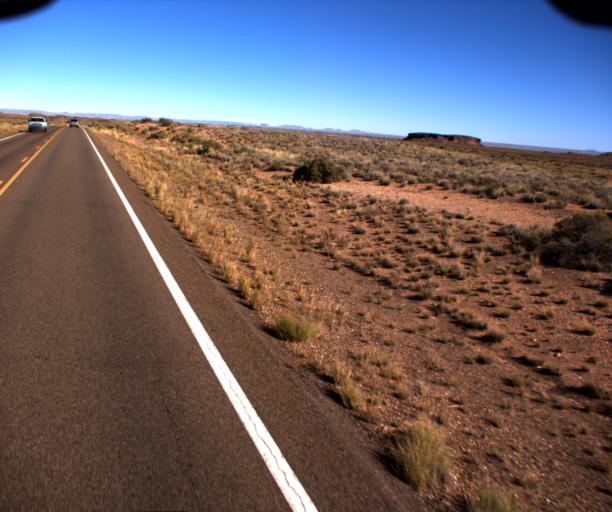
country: US
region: Arizona
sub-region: Navajo County
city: Holbrook
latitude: 34.8264
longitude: -110.1423
